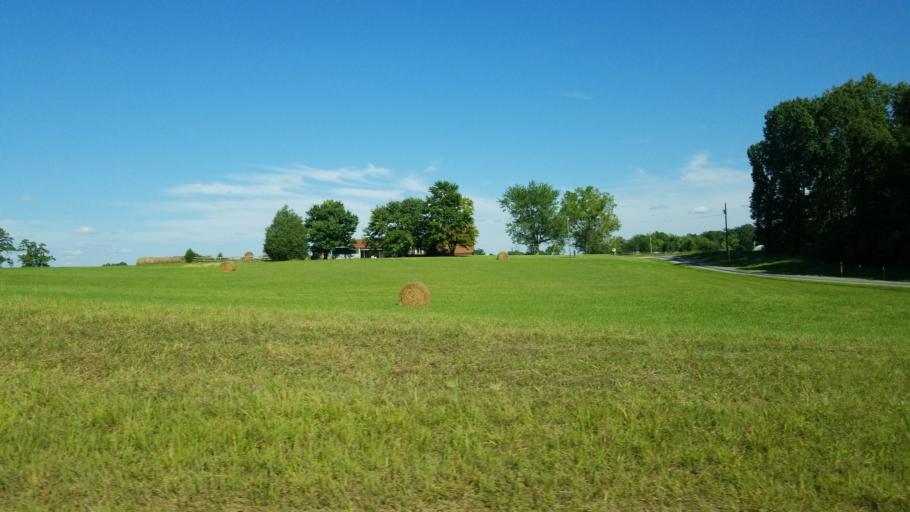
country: US
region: Illinois
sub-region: Saline County
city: Carrier Mills
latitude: 37.7992
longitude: -88.7163
